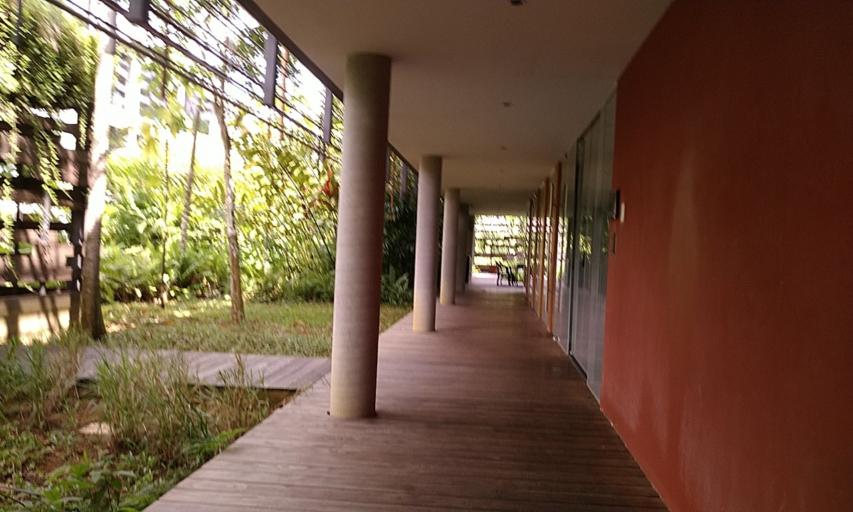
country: SG
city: Singapore
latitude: 1.2873
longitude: 103.8150
